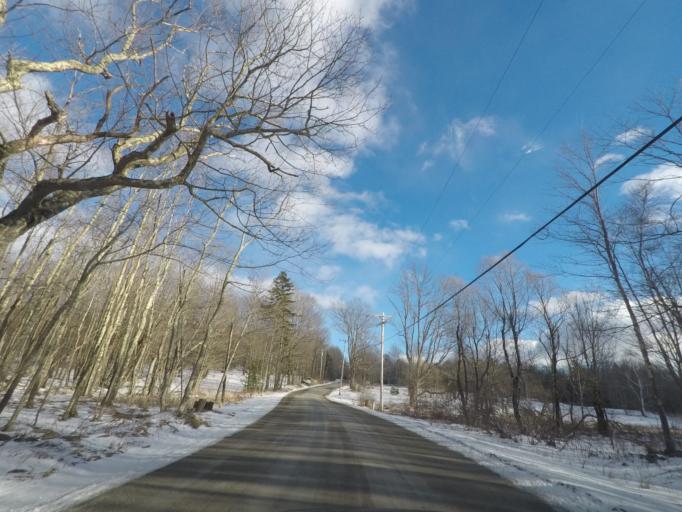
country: US
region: New York
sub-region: Rensselaer County
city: Poestenkill
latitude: 42.7462
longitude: -73.4806
